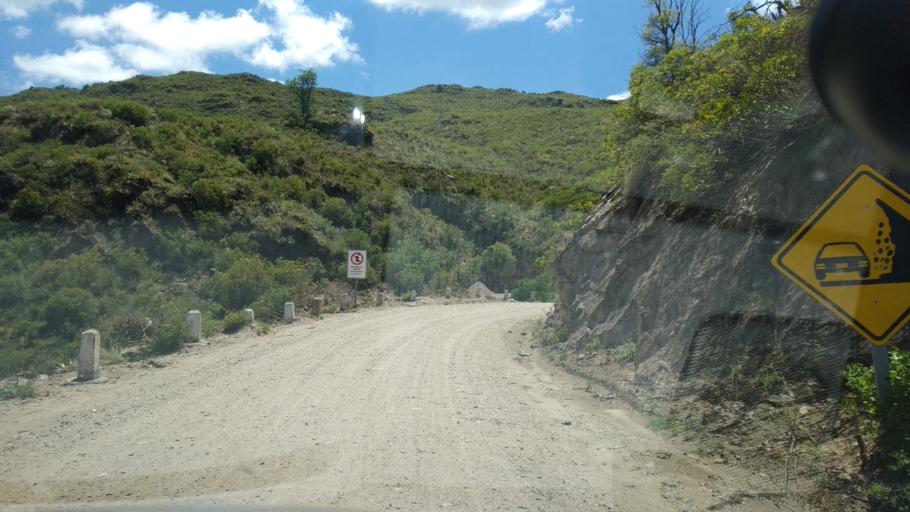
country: AR
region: Cordoba
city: Salsacate
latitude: -31.3784
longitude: -65.4012
